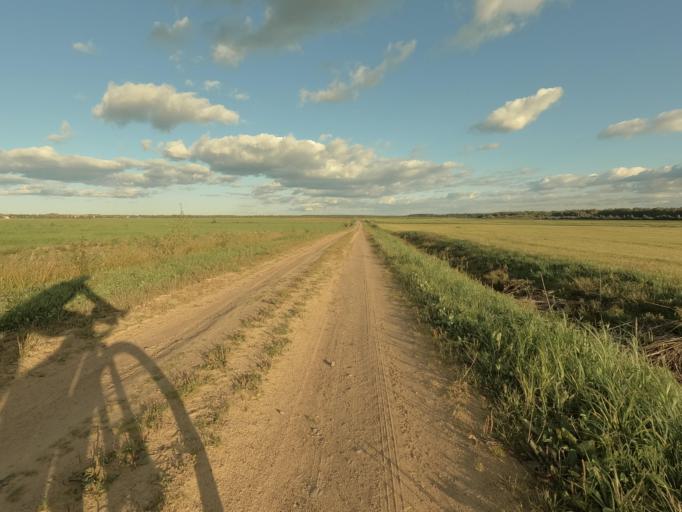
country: RU
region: Leningrad
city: Imeni Sverdlova
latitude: 59.8639
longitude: 30.7410
